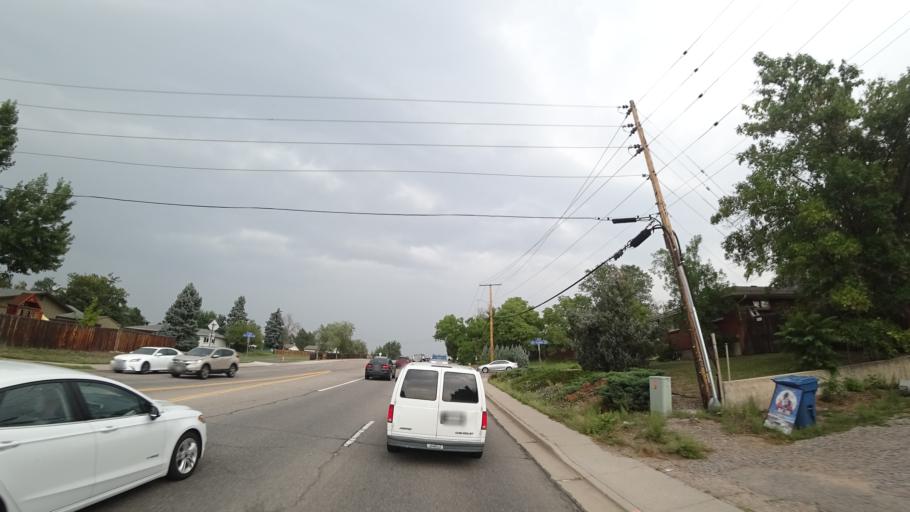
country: US
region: Colorado
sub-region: Arapahoe County
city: Greenwood Village
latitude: 39.6033
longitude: -104.9600
